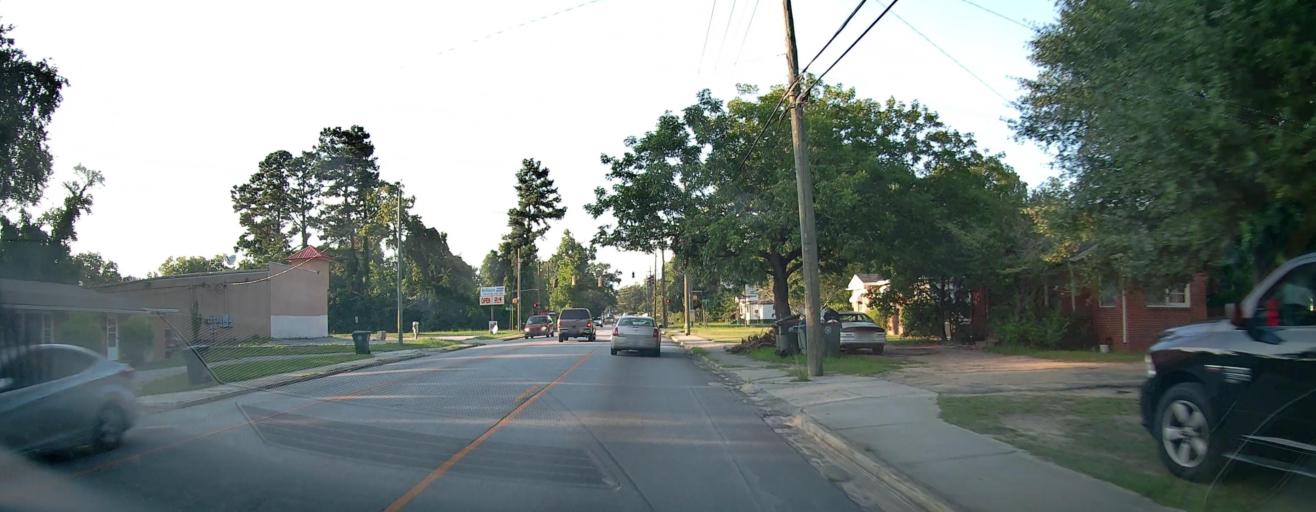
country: US
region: Georgia
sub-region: Bibb County
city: Macon
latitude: 32.8462
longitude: -83.6882
